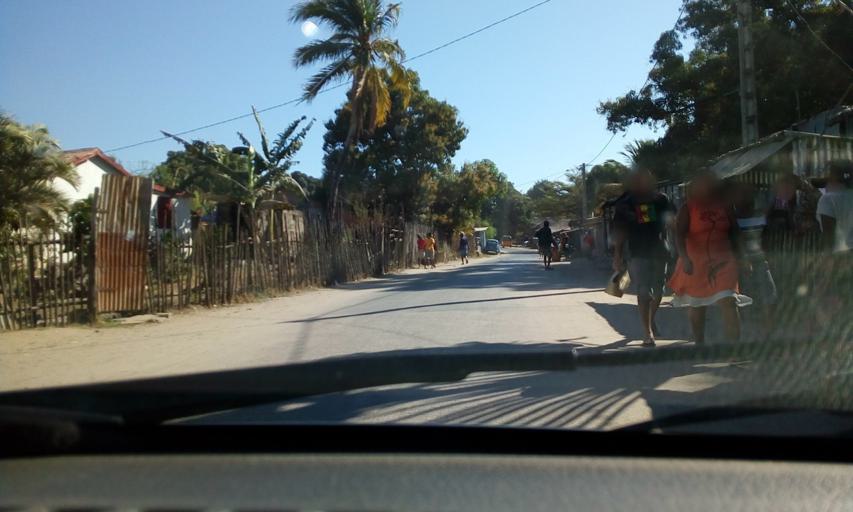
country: MG
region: Boeny
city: Mahajanga
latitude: -15.7131
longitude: 46.3385
